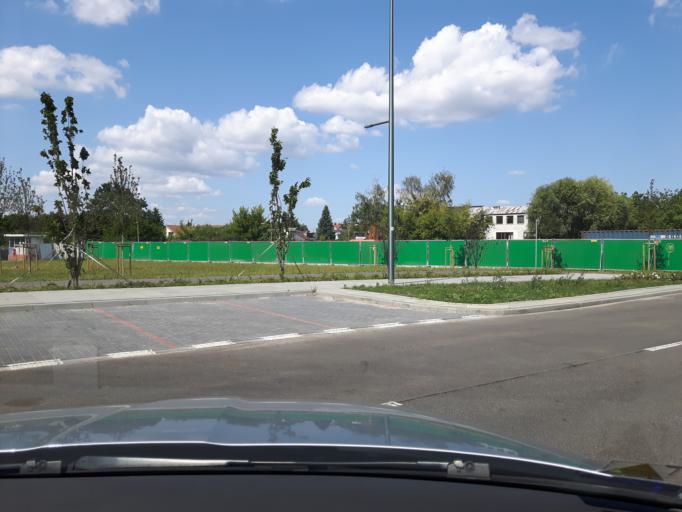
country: PL
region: Masovian Voivodeship
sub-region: Warszawa
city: Targowek
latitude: 52.2769
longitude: 21.0582
